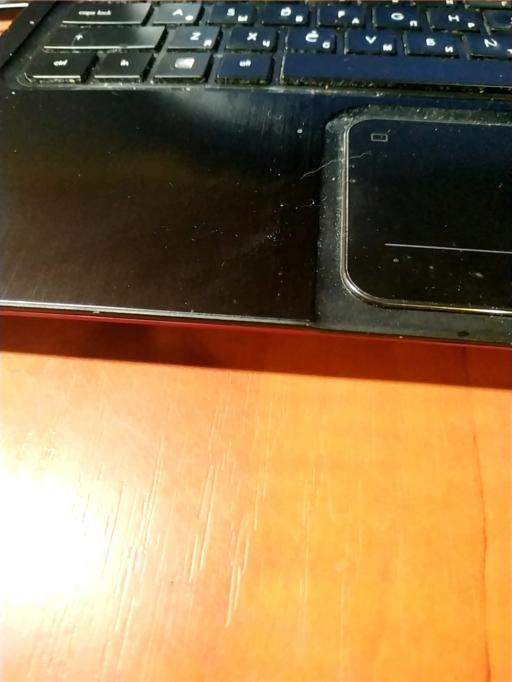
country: RU
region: Tverskaya
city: Ves'yegonsk
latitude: 58.7979
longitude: 37.5436
